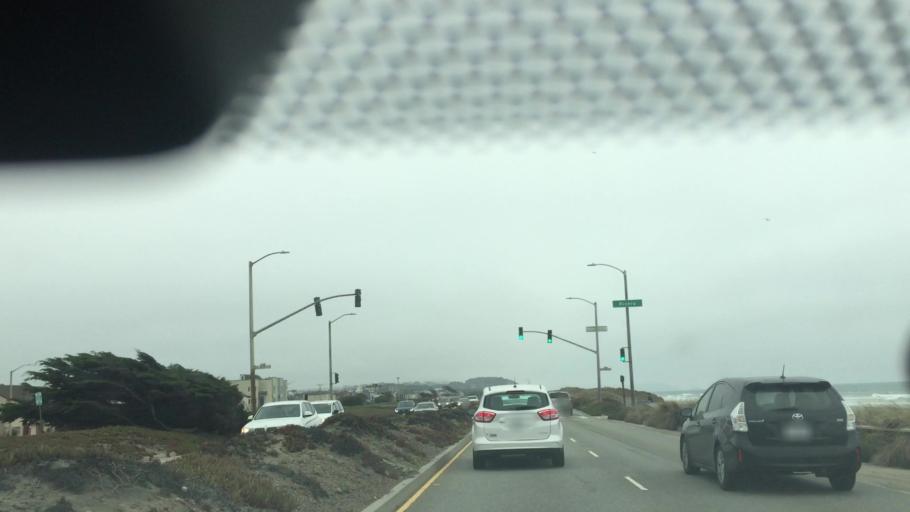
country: US
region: California
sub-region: San Mateo County
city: Daly City
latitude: 37.7459
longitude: -122.5081
